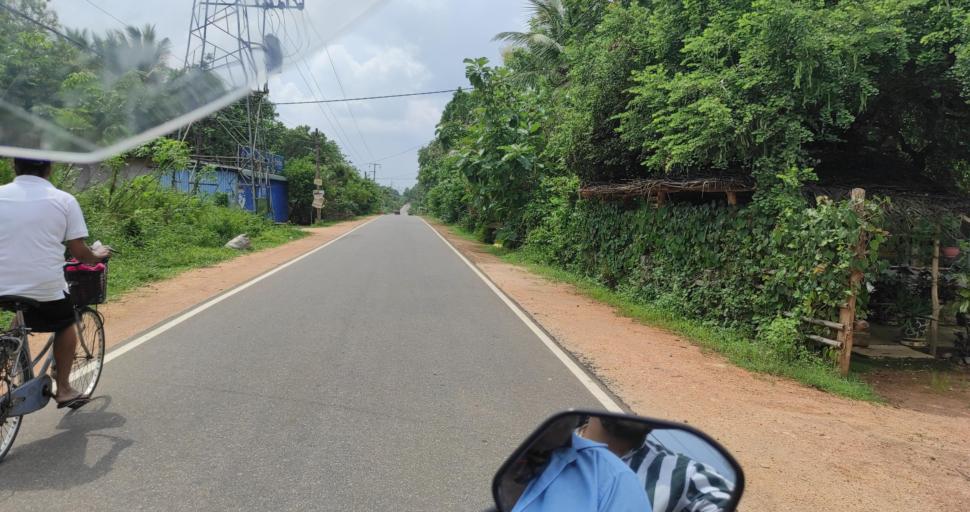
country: LK
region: Eastern Province
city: Trincomalee
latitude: 8.3757
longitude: 81.0136
